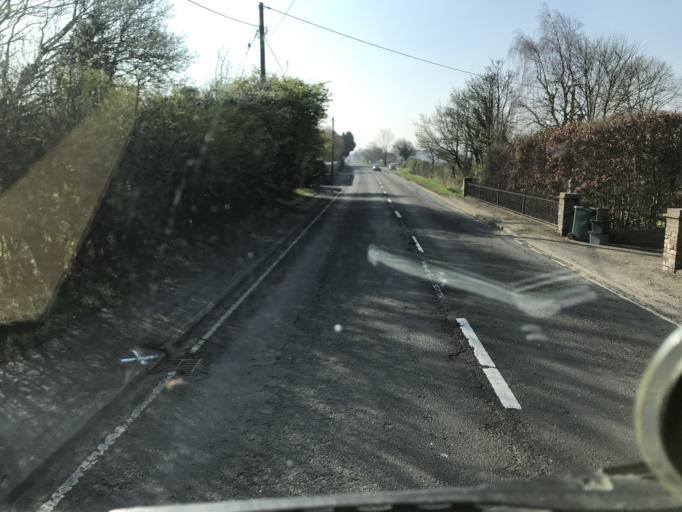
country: GB
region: England
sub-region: Cheshire West and Chester
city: Waverton
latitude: 53.1549
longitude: -2.8123
